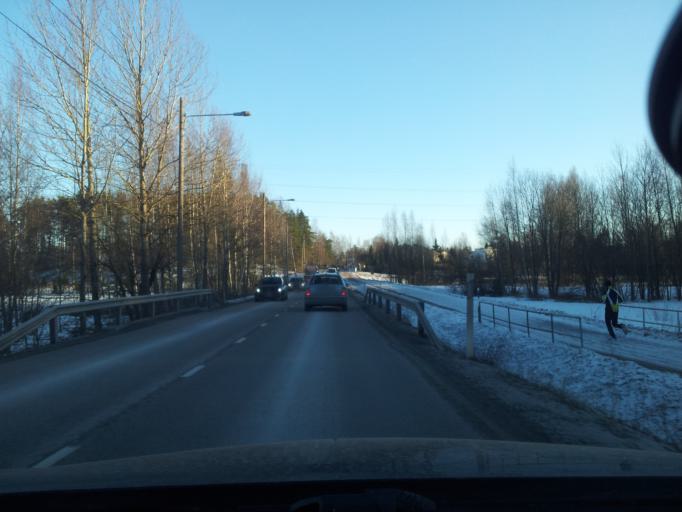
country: FI
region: Uusimaa
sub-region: Helsinki
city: Espoo
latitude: 60.1788
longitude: 24.6824
